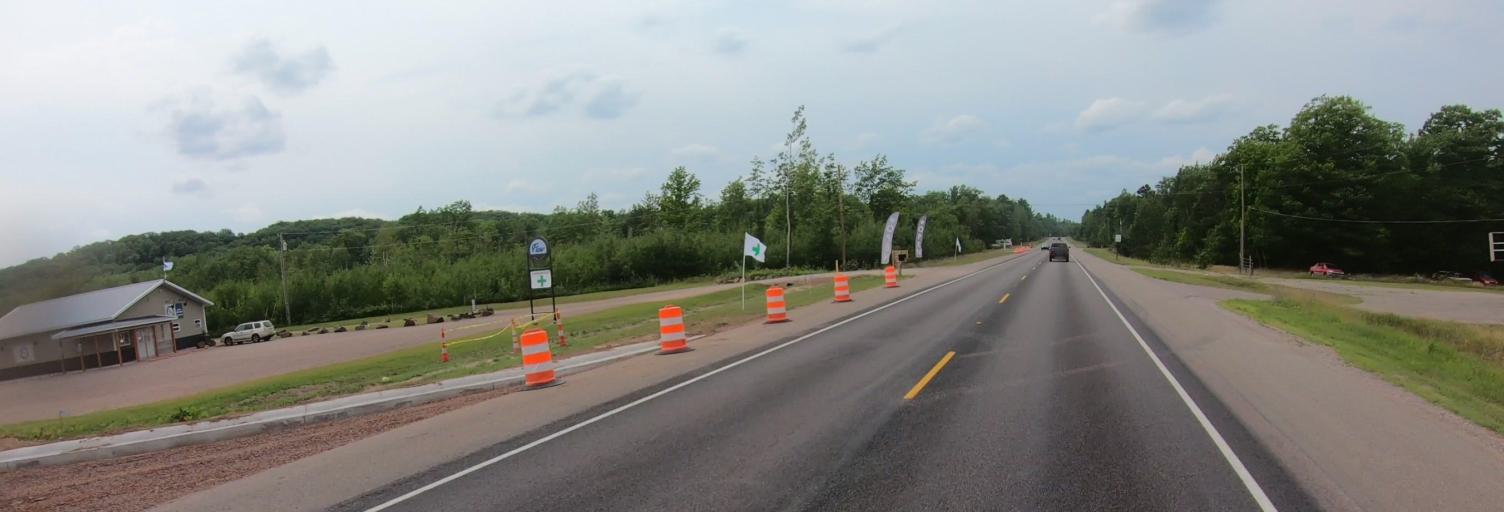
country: US
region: Michigan
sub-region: Marquette County
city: Harvey
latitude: 46.4658
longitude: -87.4296
